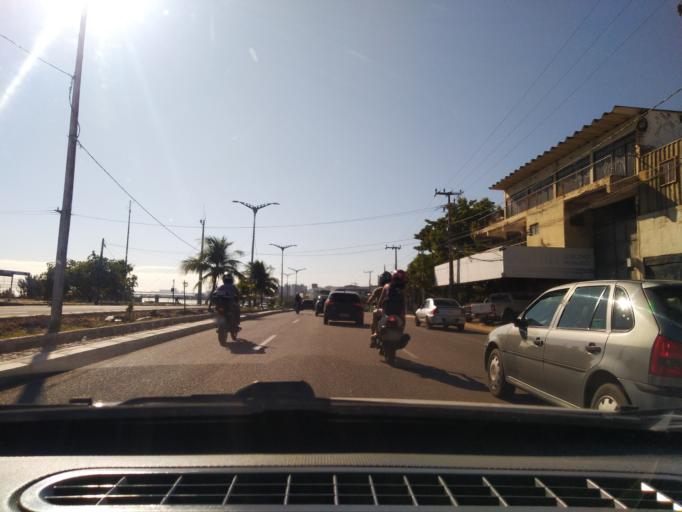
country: BR
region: Ceara
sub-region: Fortaleza
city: Fortaleza
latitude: -3.7180
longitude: -38.5382
